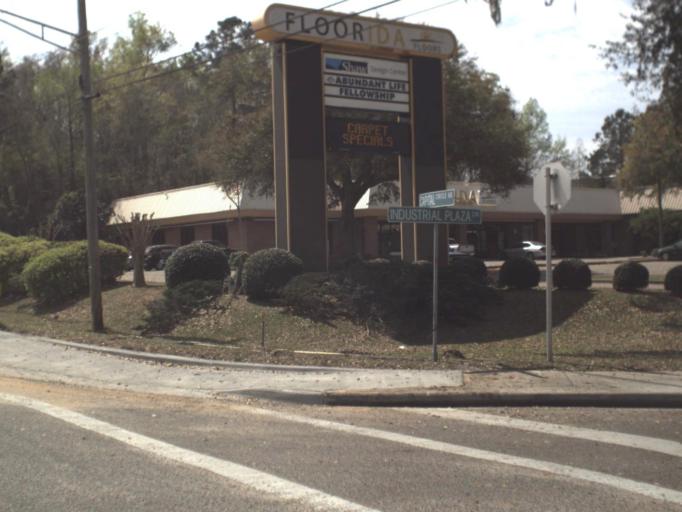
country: US
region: Florida
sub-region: Leon County
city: Tallahassee
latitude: 30.4502
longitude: -84.2266
